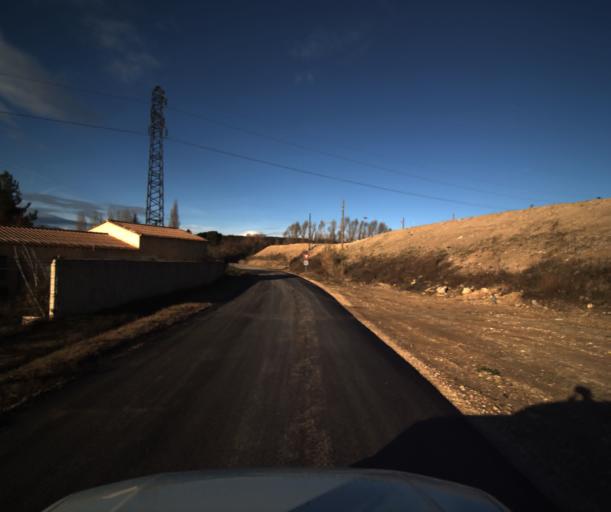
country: FR
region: Provence-Alpes-Cote d'Azur
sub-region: Departement du Vaucluse
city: Pertuis
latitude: 43.6905
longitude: 5.4825
